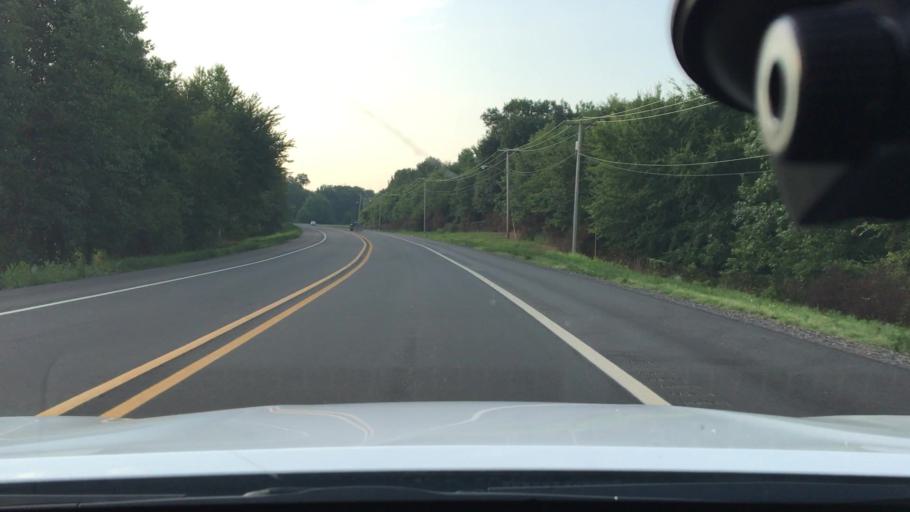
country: US
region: Arkansas
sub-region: Johnson County
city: Clarksville
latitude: 35.4541
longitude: -93.5332
